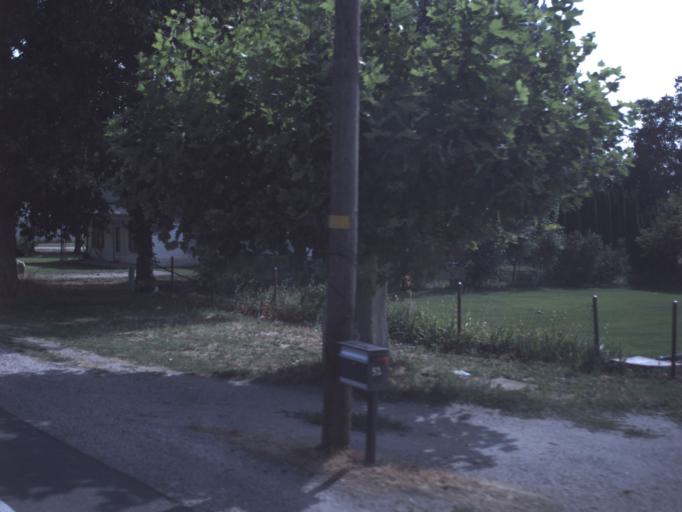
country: US
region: Utah
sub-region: Box Elder County
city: Willard
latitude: 41.4077
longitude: -112.0364
